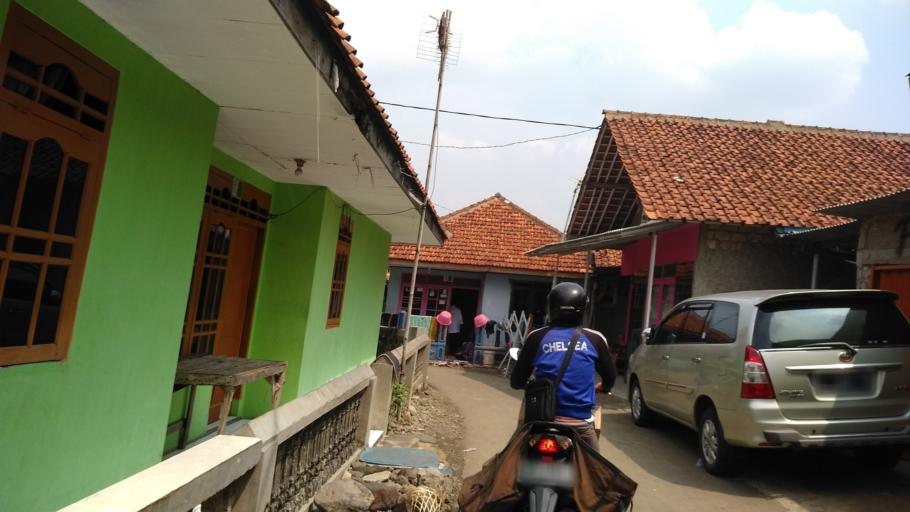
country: ID
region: West Java
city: Ciampea
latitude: -6.5602
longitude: 106.7456
